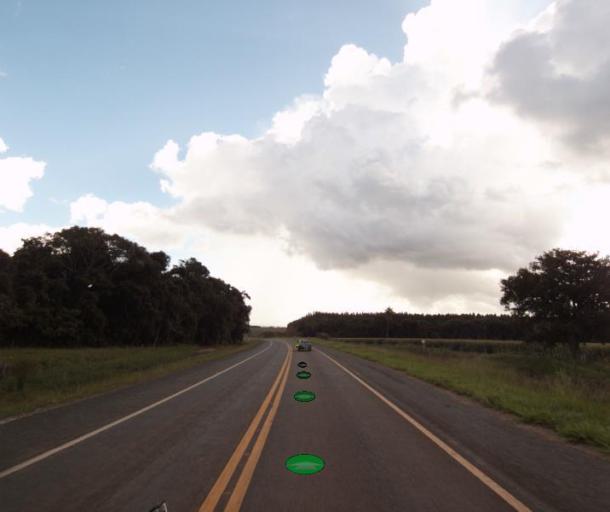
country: BR
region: Goias
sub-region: Itaberai
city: Itaberai
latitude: -15.9852
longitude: -49.7053
